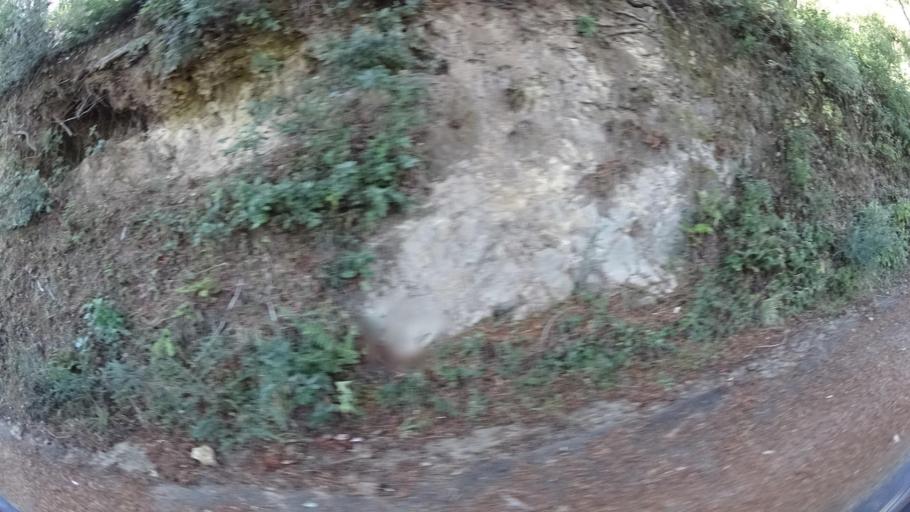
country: US
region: California
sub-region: Monterey County
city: Carmel Valley Village
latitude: 36.3758
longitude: -121.8550
